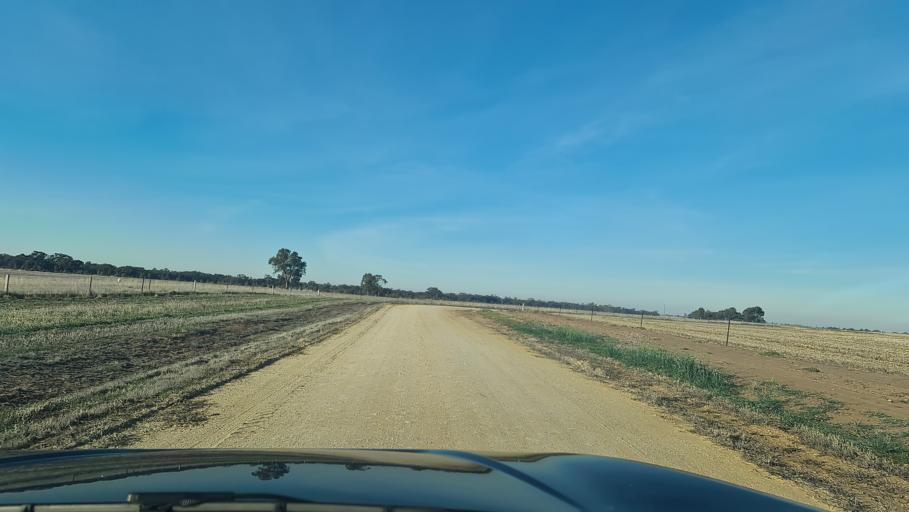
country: AU
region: Victoria
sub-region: Horsham
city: Horsham
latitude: -36.3603
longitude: 142.3965
